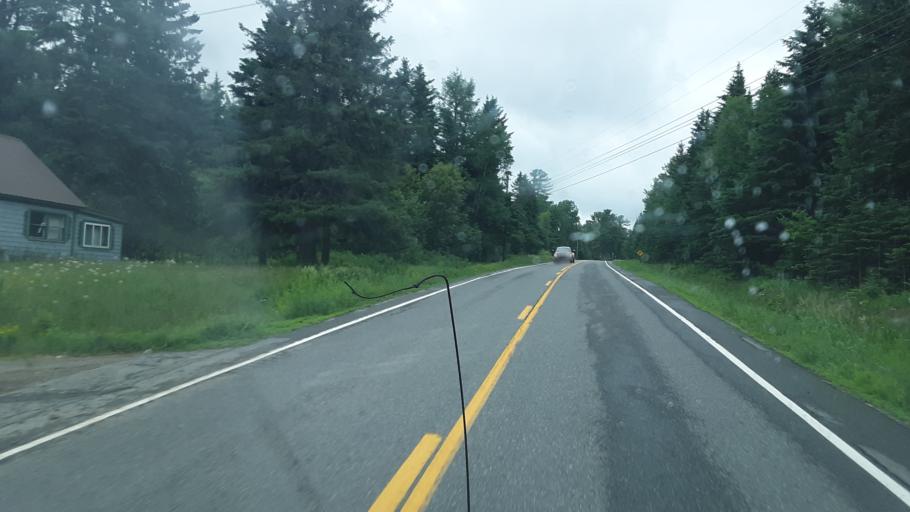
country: US
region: Maine
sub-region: Aroostook County
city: Presque Isle
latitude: 46.4753
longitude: -68.3882
